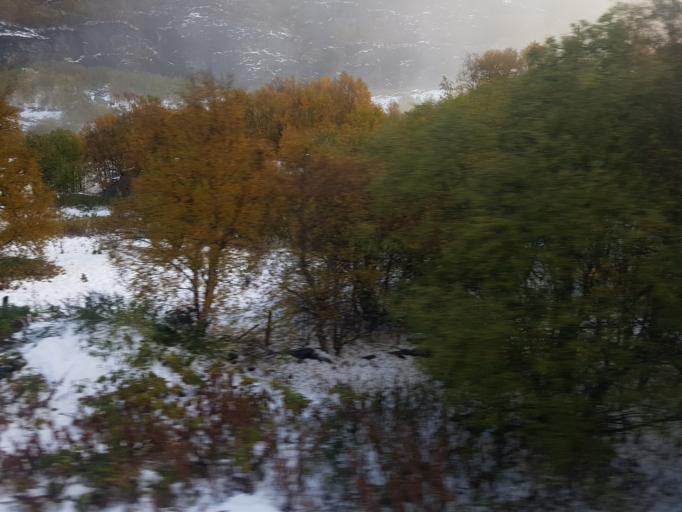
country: NO
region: Sor-Trondelag
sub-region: Oppdal
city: Oppdal
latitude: 62.4429
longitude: 9.5985
